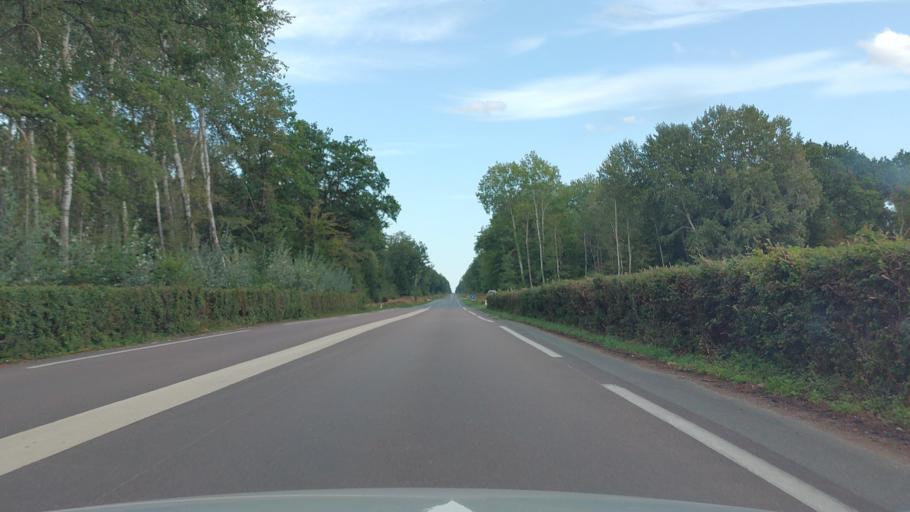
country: FR
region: Ile-de-France
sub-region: Departement de Seine-et-Marne
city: Le Chatelet-en-Brie
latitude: 48.5424
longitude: 2.8136
